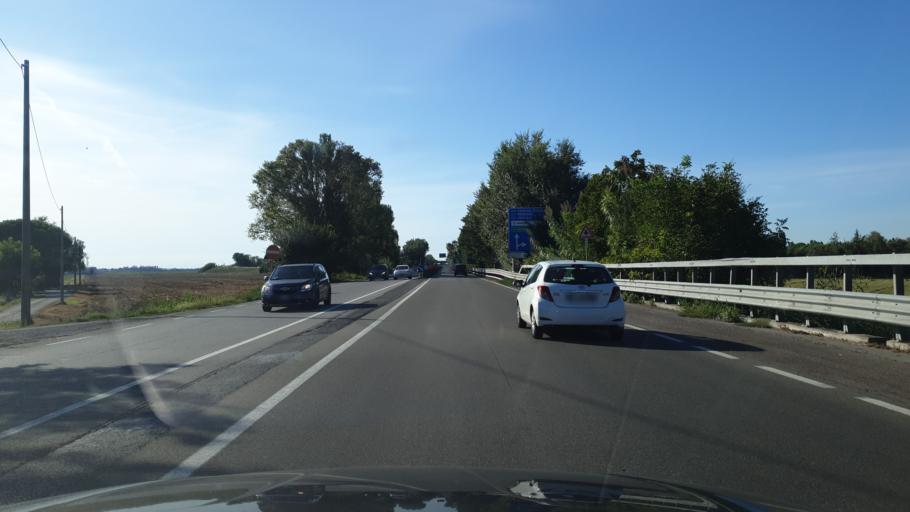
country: IT
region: Emilia-Romagna
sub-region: Provincia di Ravenna
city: Classe
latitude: 44.3691
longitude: 12.2449
